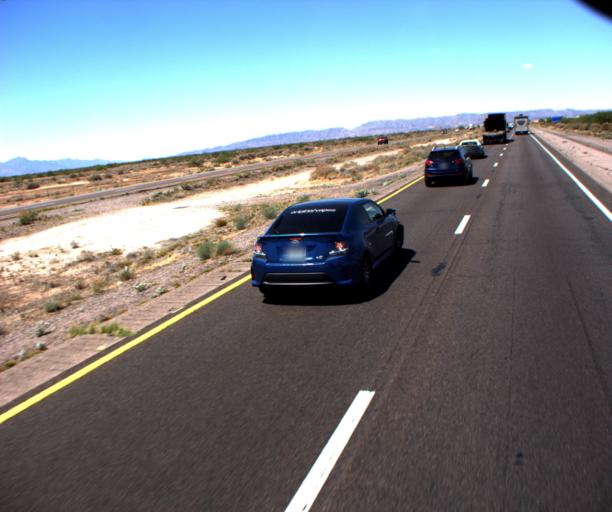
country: US
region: Arizona
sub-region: Maricopa County
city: Sun Lakes
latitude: 33.2065
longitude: -111.9101
